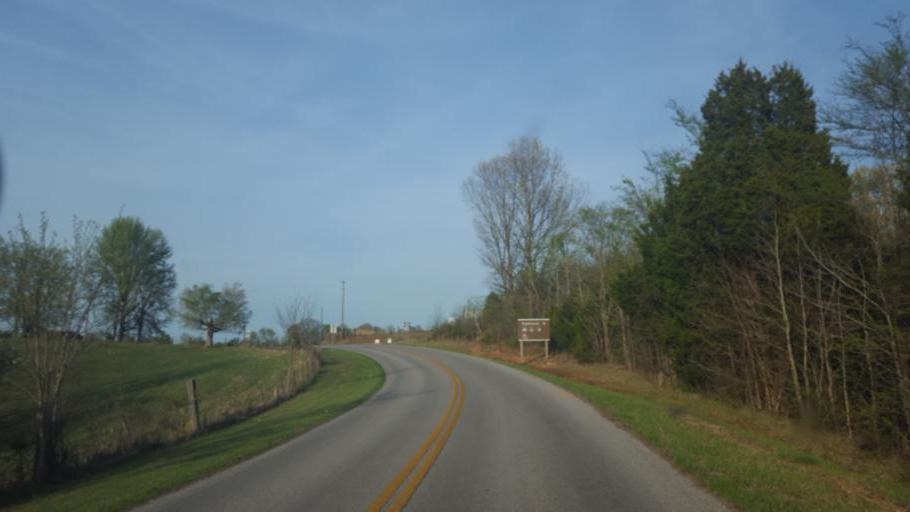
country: US
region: Kentucky
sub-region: Allen County
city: Scottsville
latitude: 36.9108
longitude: -86.1087
